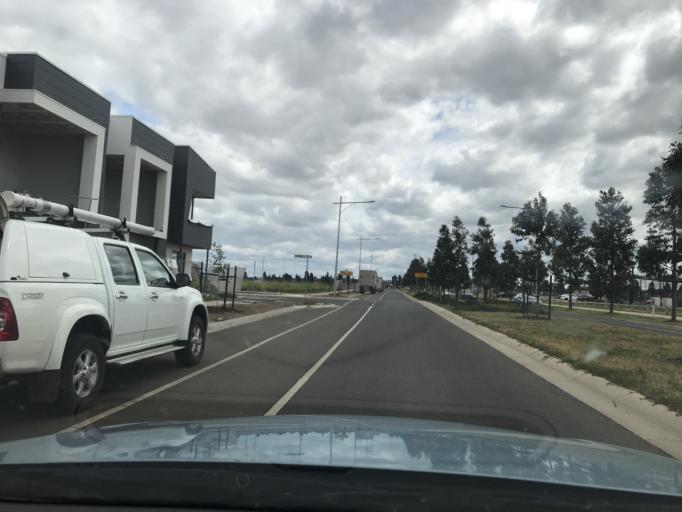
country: AU
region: Victoria
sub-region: Wyndham
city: Williams Landing
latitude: -37.8623
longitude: 144.7515
